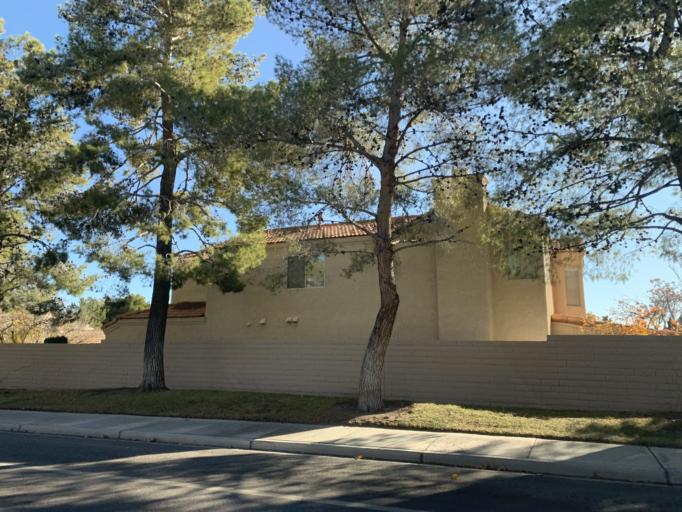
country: US
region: Nevada
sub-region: Clark County
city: Summerlin South
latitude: 36.1335
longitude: -115.3076
